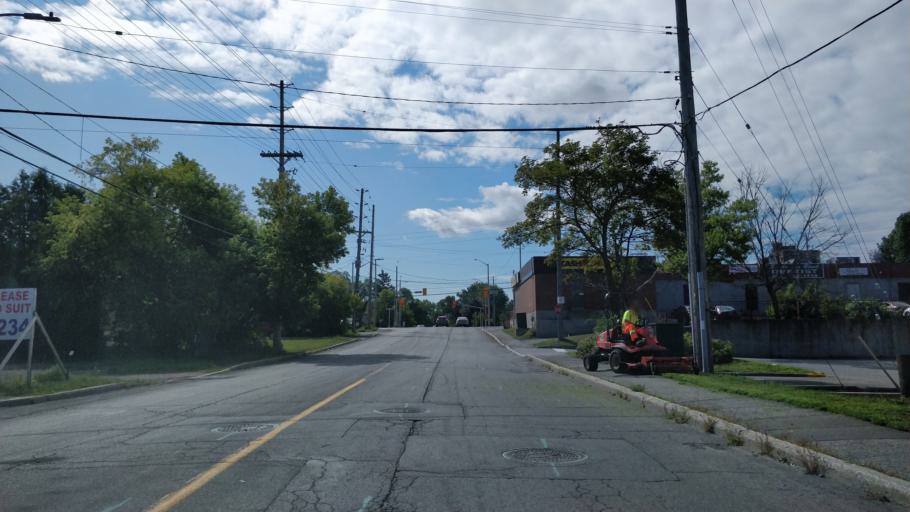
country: CA
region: Ontario
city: Ottawa
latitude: 45.3550
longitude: -75.6436
